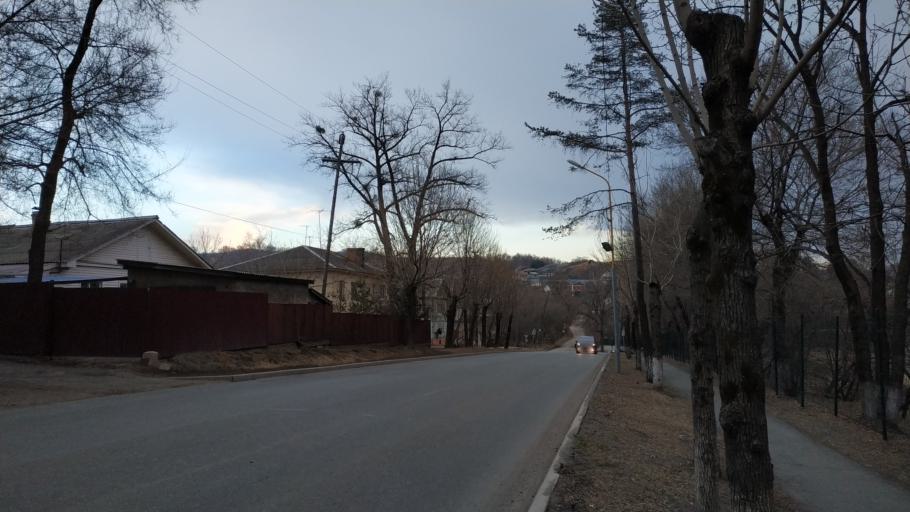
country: RU
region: Primorskiy
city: Artem
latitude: 43.3542
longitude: 132.1912
